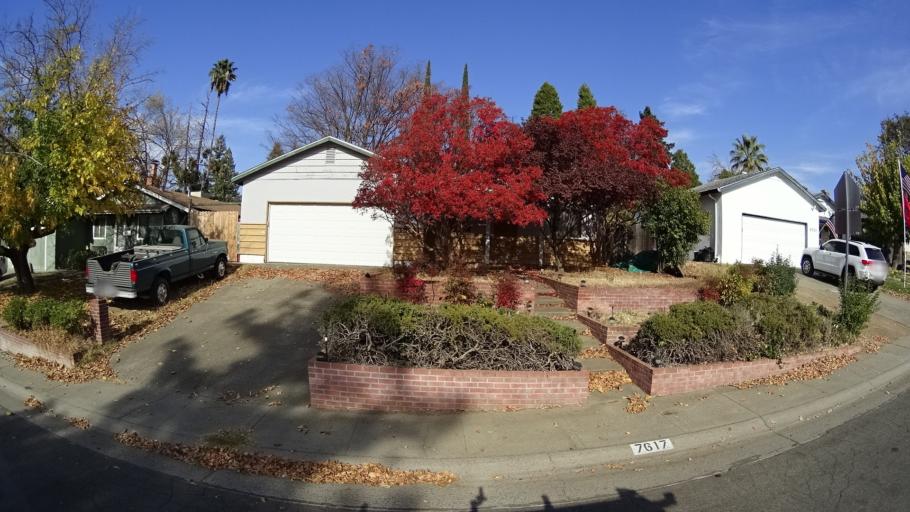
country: US
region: California
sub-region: Sacramento County
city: Fair Oaks
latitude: 38.6697
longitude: -121.2833
